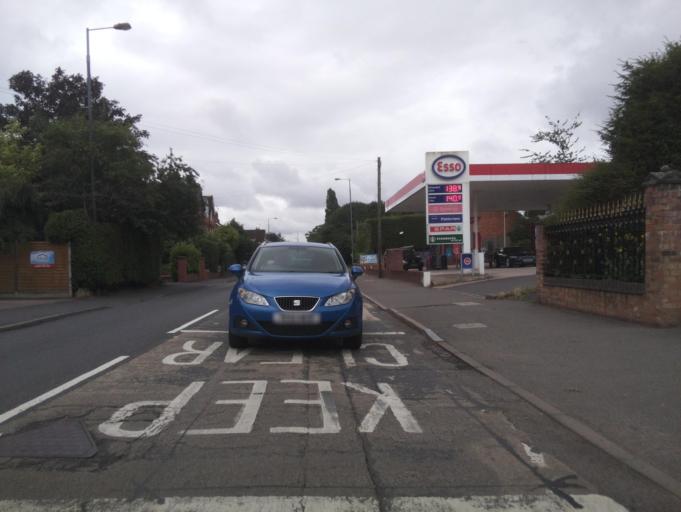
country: GB
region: England
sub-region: Worcestershire
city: Droitwich
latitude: 52.2613
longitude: -2.1528
